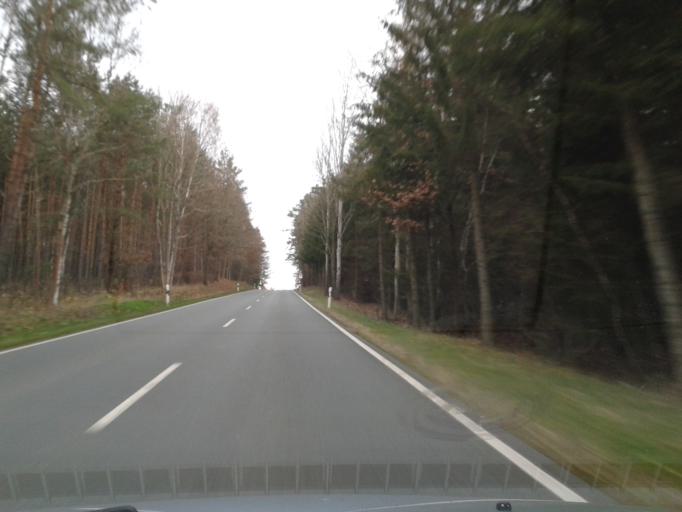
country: DE
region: Thuringia
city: Hainspitz
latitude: 50.9247
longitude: 11.8318
